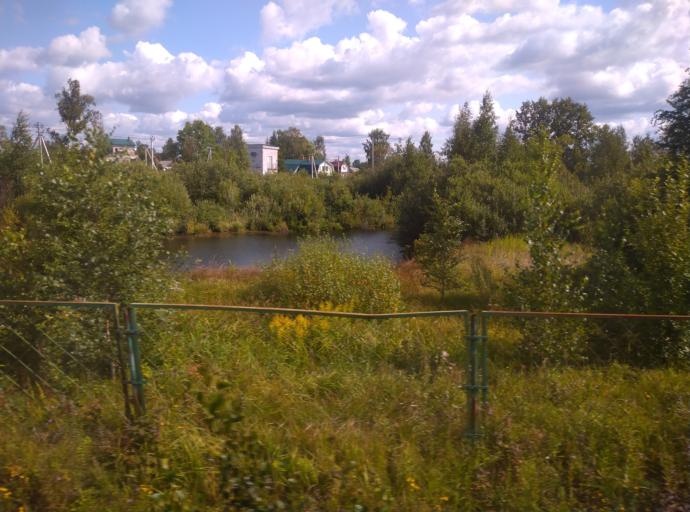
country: RU
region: Leningrad
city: Krasnyy Bor
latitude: 59.6812
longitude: 30.7000
